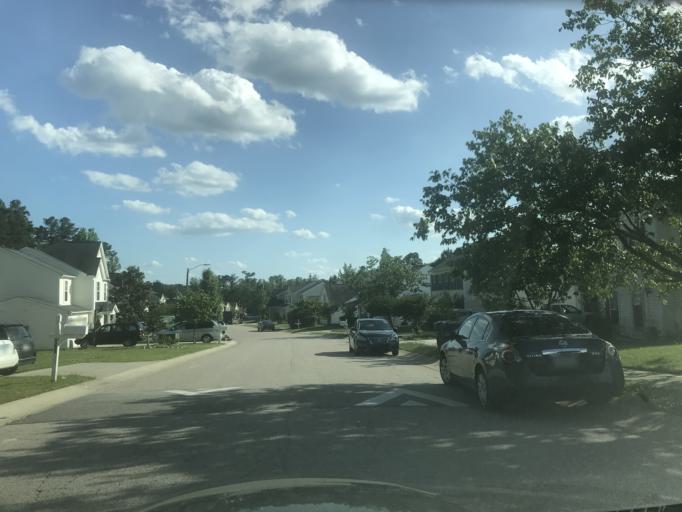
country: US
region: North Carolina
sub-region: Wake County
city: Knightdale
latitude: 35.8473
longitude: -78.5513
